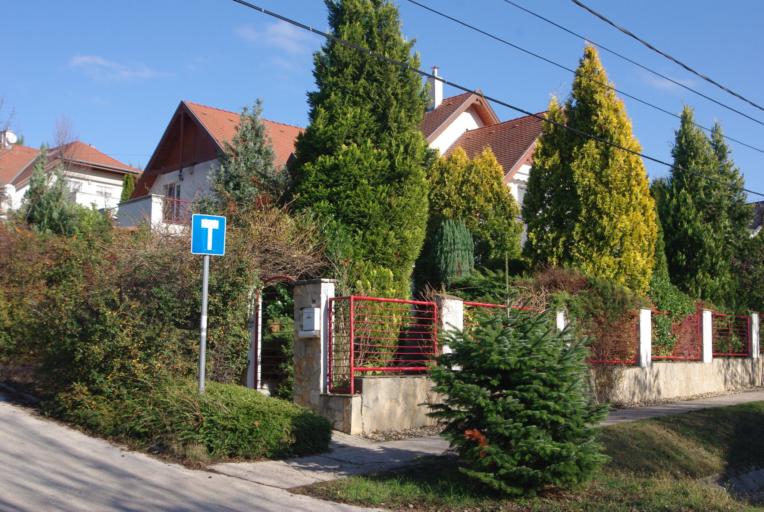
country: HU
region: Pest
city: Urom
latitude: 47.5898
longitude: 19.0270
